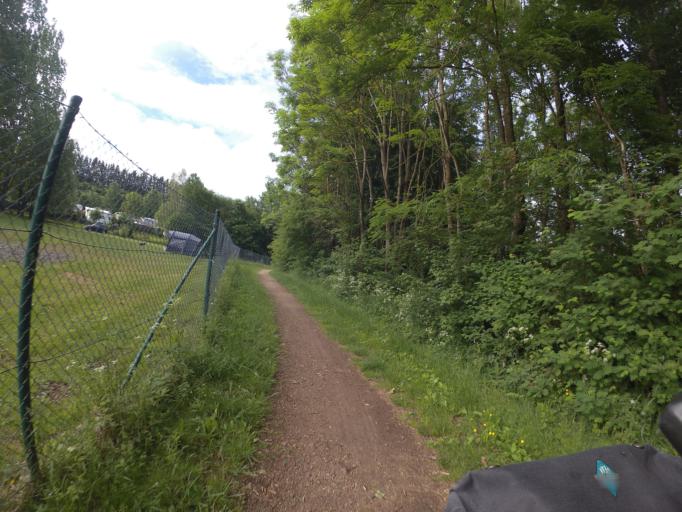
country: DE
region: Rheinland-Pfalz
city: Hallschlag
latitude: 50.3625
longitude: 6.4523
